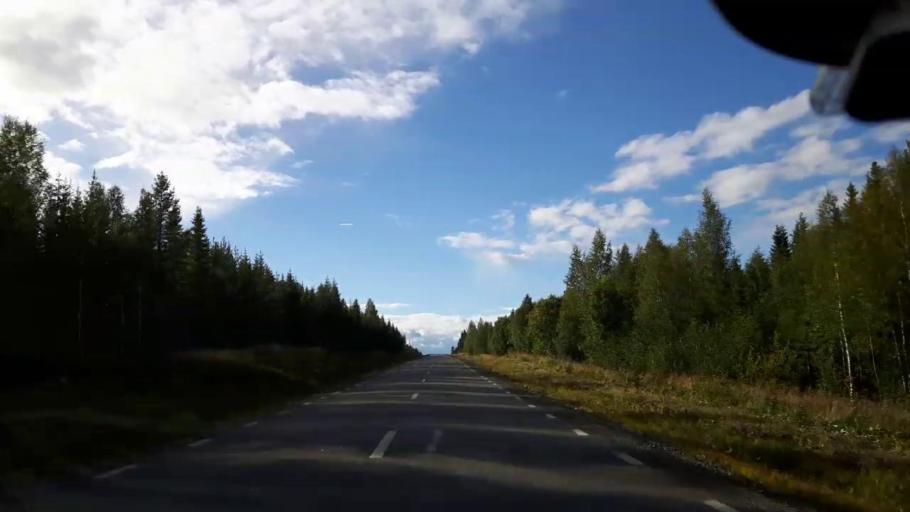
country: SE
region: Jaemtland
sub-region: Stroemsunds Kommun
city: Stroemsund
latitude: 63.5736
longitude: 15.7586
